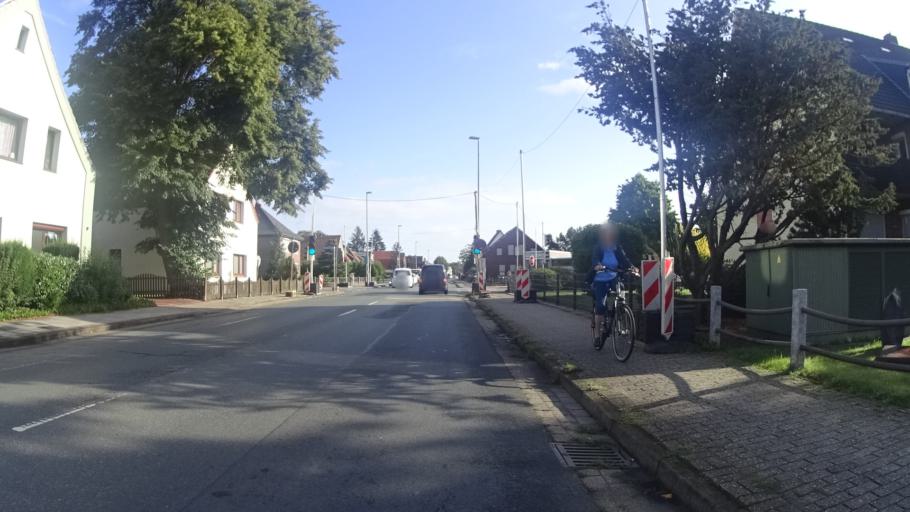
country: DE
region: Lower Saxony
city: Nordenham
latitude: 53.4969
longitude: 8.4750
